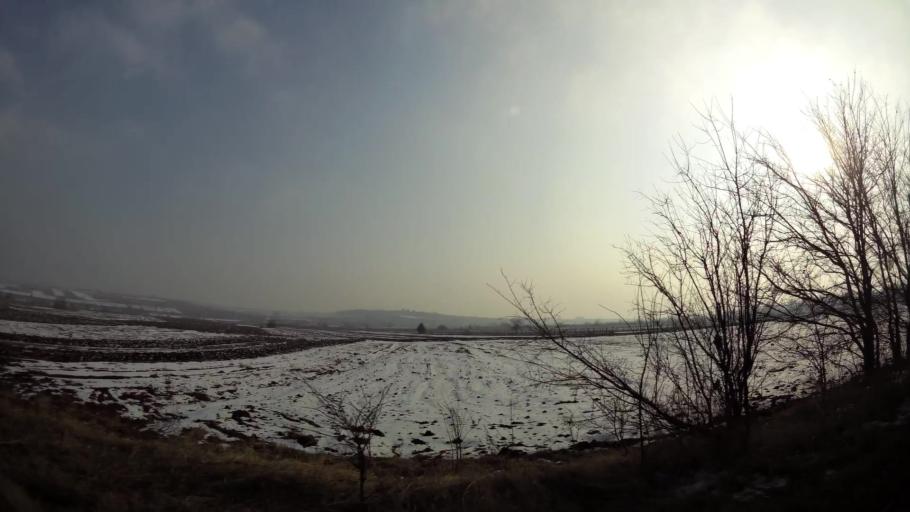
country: MK
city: Miladinovci
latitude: 41.9729
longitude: 21.6364
